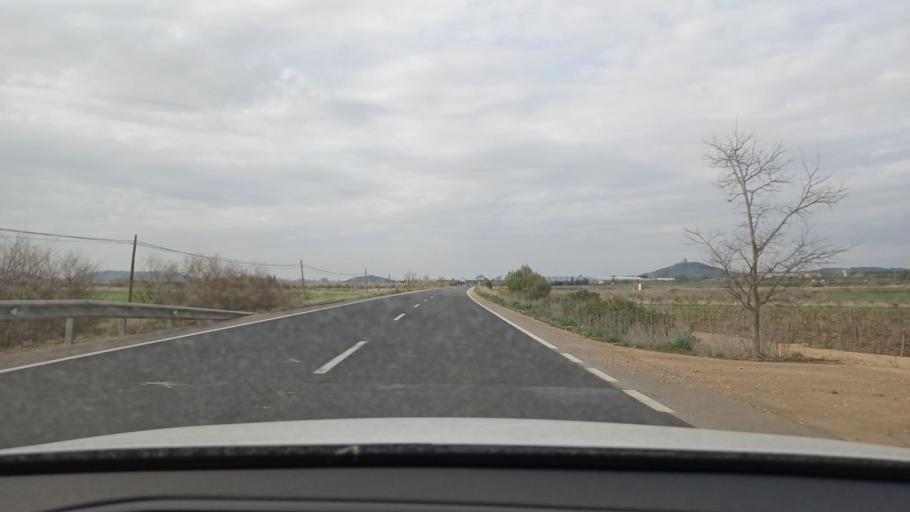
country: ES
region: Catalonia
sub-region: Provincia de Tarragona
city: Ulldecona
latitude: 40.6143
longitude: 0.4660
